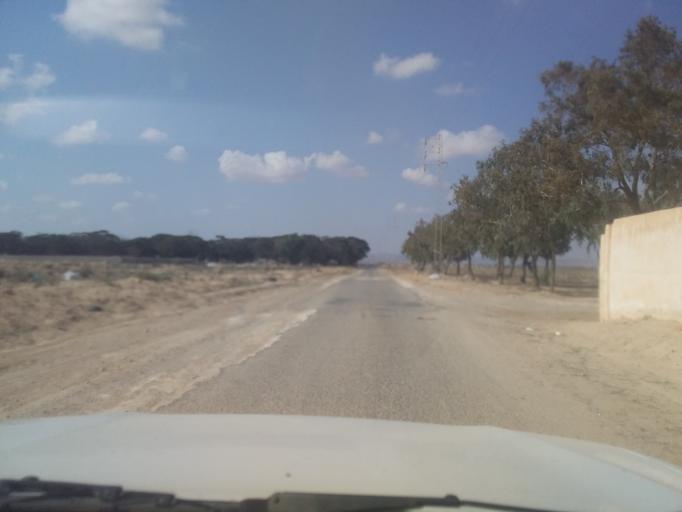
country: TN
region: Qabis
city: Gabes
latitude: 33.6304
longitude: 10.2729
